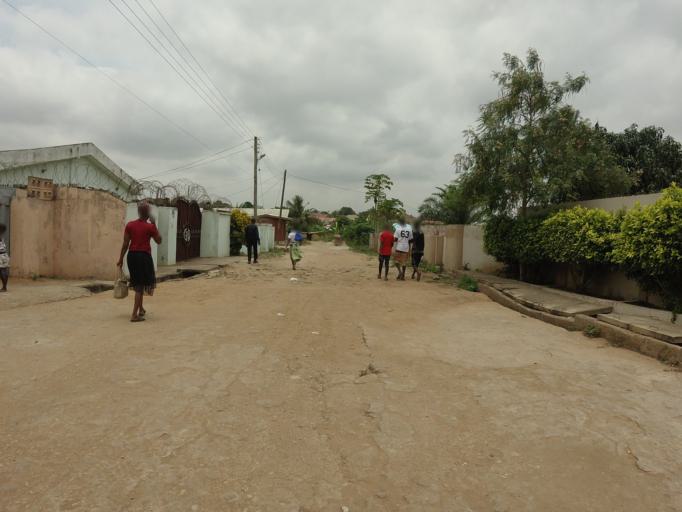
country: GH
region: Greater Accra
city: Dome
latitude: 5.6365
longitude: -0.2319
